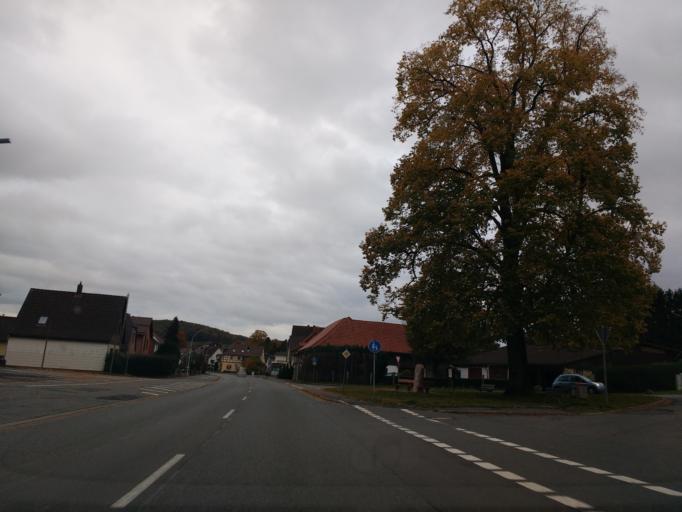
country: DE
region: Lower Saxony
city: Bad Lauterberg im Harz
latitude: 51.6161
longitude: 10.4172
